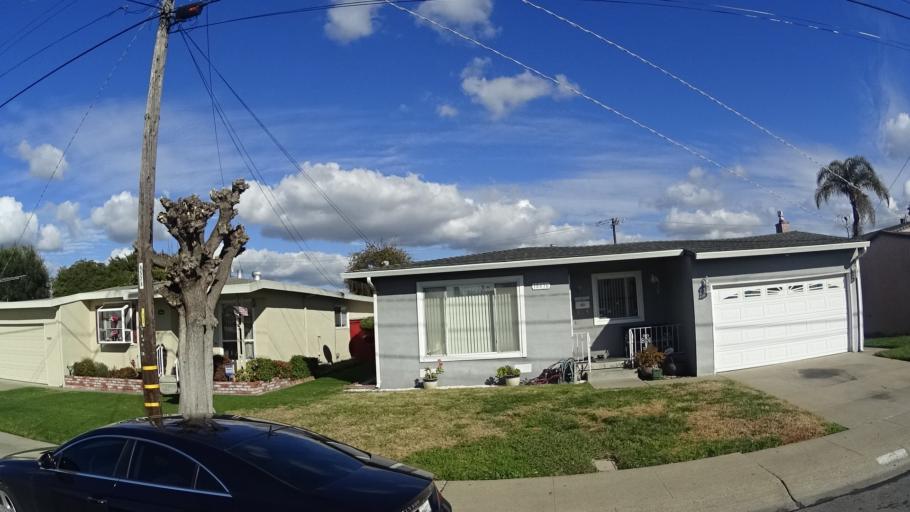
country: US
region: California
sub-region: Alameda County
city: San Lorenzo
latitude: 37.6735
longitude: -122.1198
